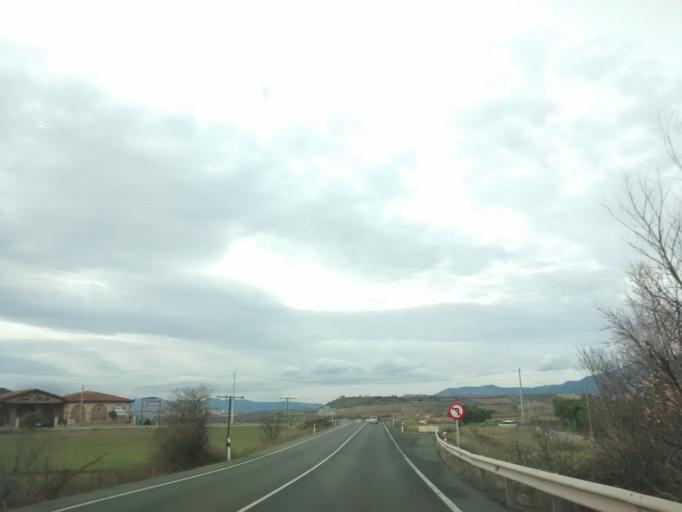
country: ES
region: La Rioja
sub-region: Provincia de La Rioja
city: San Asensio
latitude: 42.5194
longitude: -2.7471
